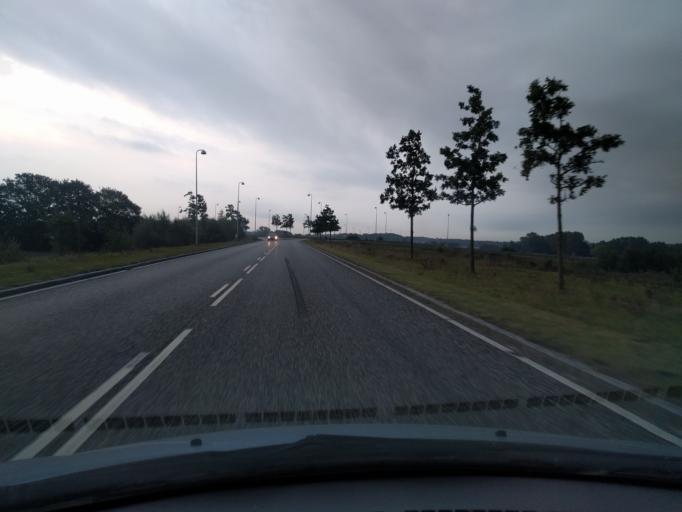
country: DK
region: South Denmark
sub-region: Odense Kommune
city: Neder Holluf
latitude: 55.3671
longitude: 10.5148
